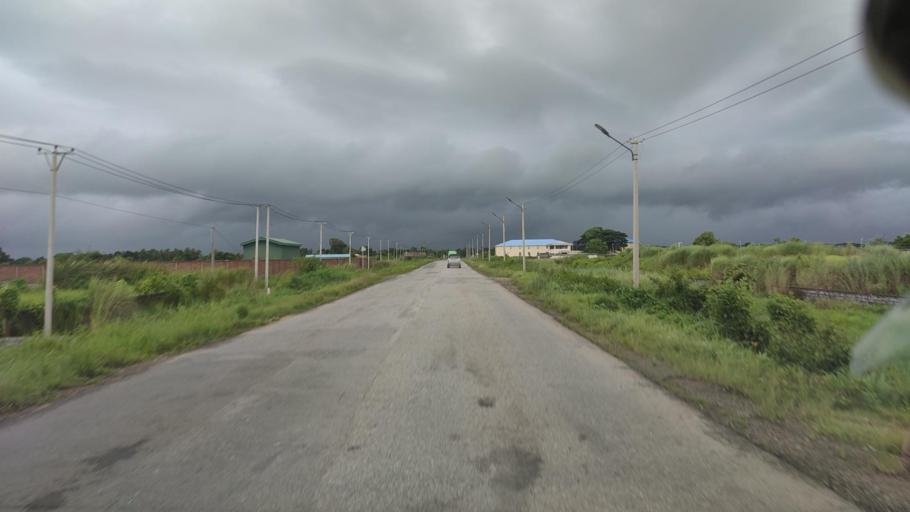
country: MM
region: Bago
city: Bago
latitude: 17.3853
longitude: 96.4904
